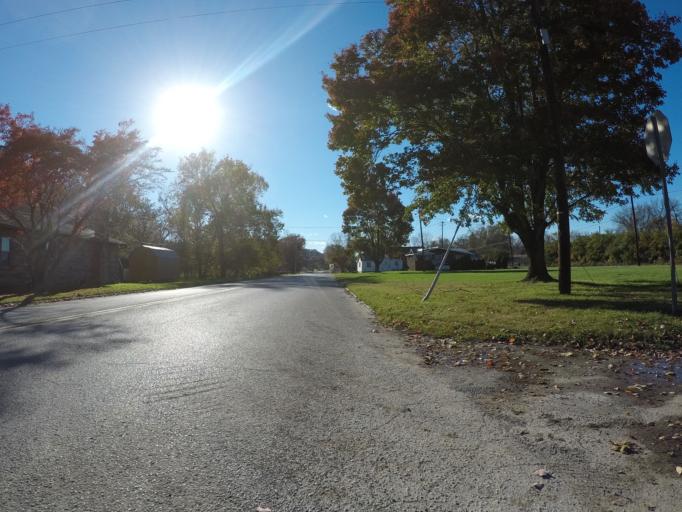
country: US
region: West Virginia
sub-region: Cabell County
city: Huntington
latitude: 38.4057
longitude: -82.4752
